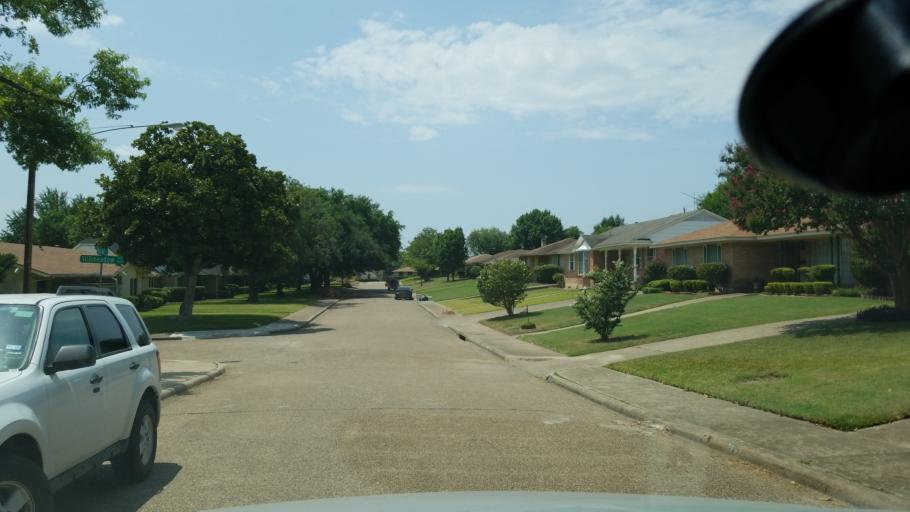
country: US
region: Texas
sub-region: Dallas County
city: Duncanville
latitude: 32.6756
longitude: -96.8393
